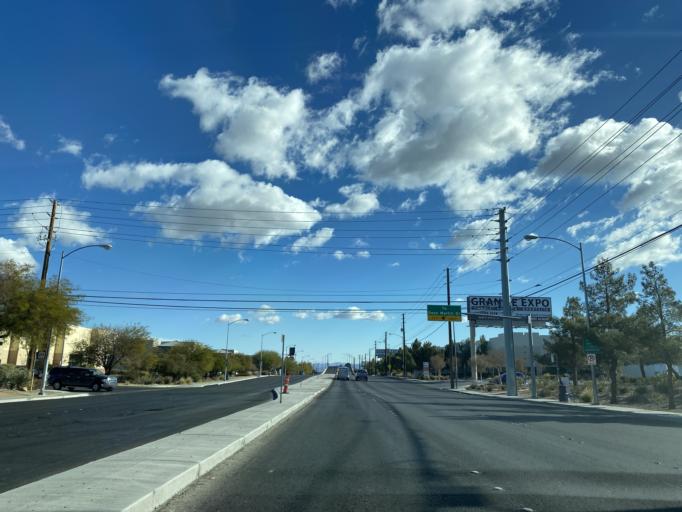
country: US
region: Nevada
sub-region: Clark County
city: Paradise
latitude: 36.0715
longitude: -115.1864
